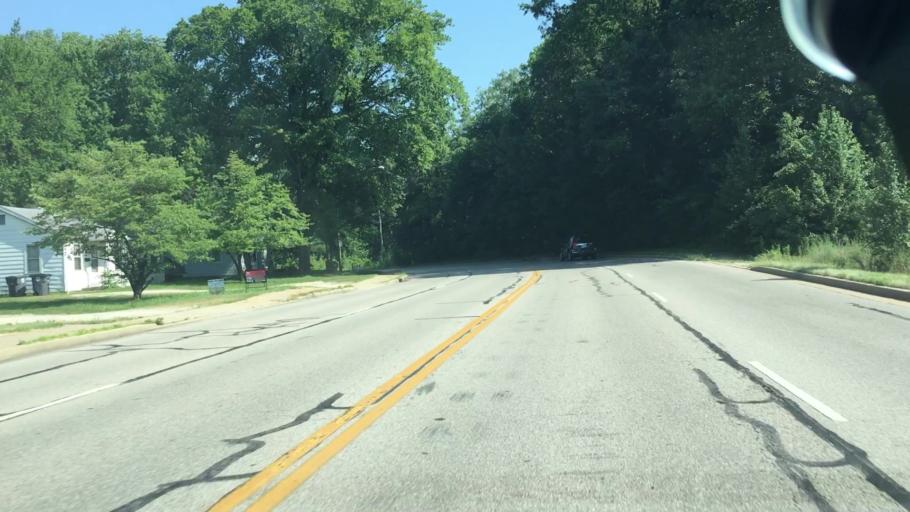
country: US
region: Indiana
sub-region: Vanderburgh County
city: Melody Hill
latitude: 37.9969
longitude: -87.5291
